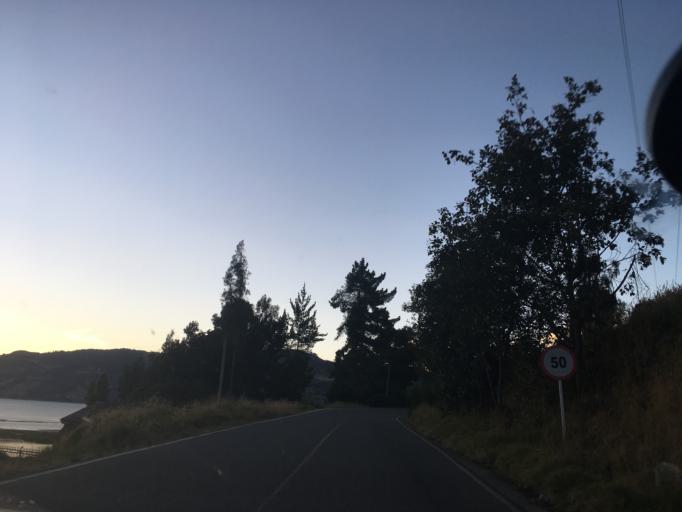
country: CO
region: Boyaca
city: Aquitania
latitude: 5.5884
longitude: -72.9015
